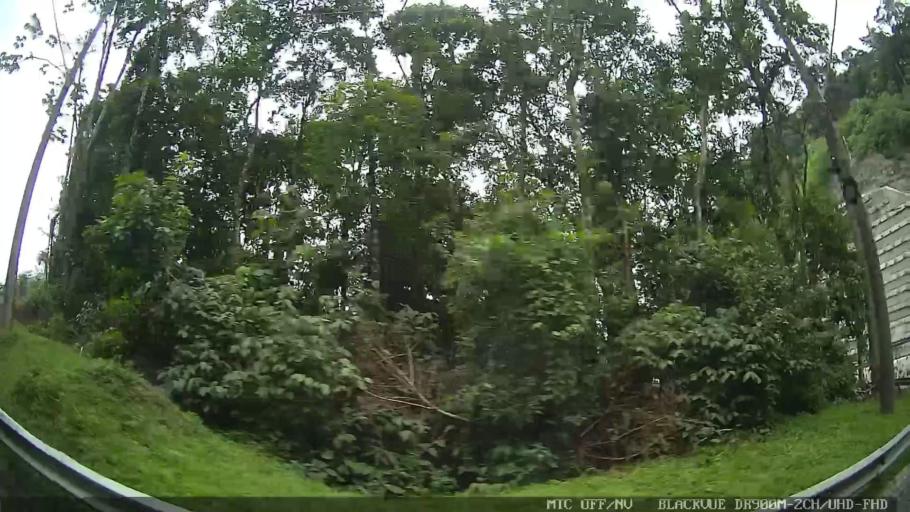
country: BR
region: Sao Paulo
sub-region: Caraguatatuba
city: Caraguatatuba
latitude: -23.5889
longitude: -45.4478
